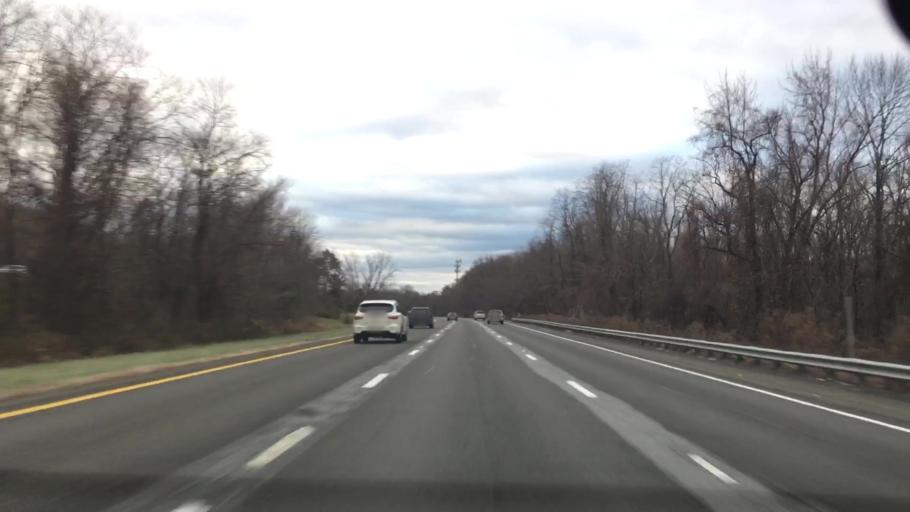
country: US
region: New York
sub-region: Westchester County
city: Armonk
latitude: 41.1680
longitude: -73.6879
